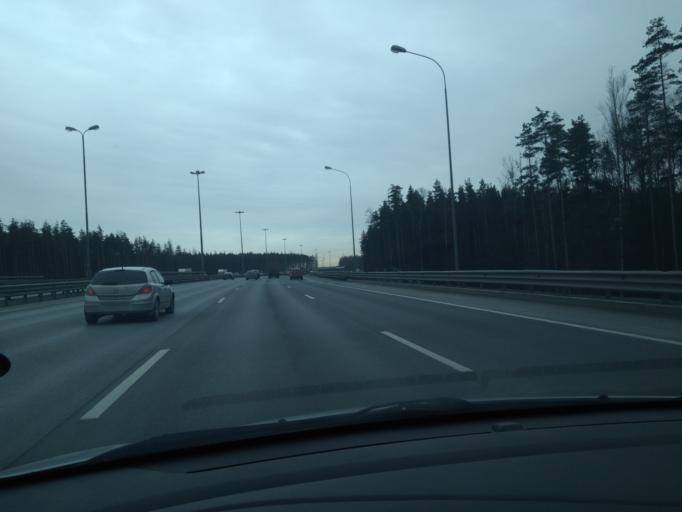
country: RU
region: Leningrad
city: Yanino Vtoroye
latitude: 59.9652
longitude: 30.5533
